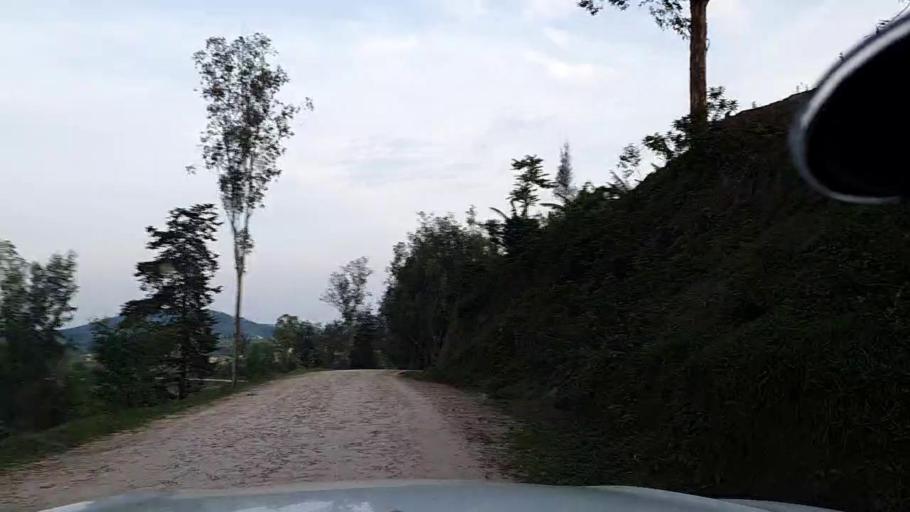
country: RW
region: Southern Province
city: Nyanza
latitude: -2.2149
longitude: 29.6353
